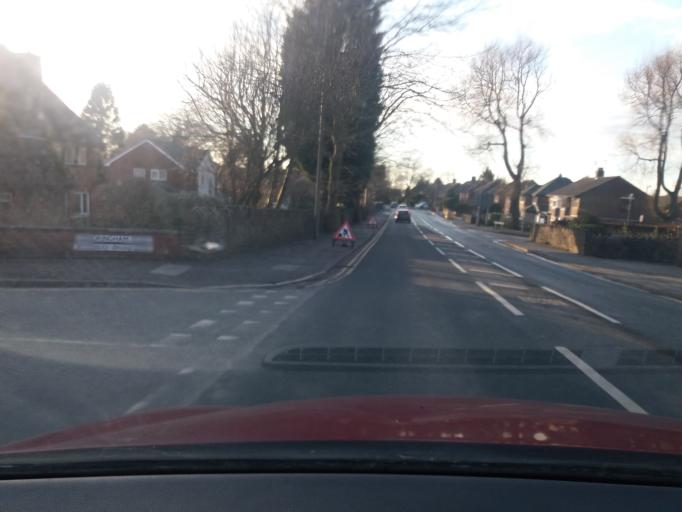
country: GB
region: England
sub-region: Lancashire
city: Chorley
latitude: 53.6542
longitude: -2.6417
